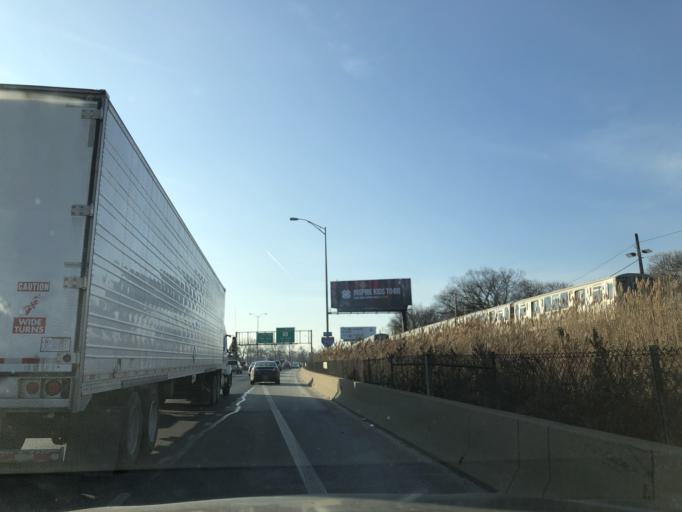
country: US
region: Illinois
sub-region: Cook County
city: Forest Park
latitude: 41.8725
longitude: -87.8192
